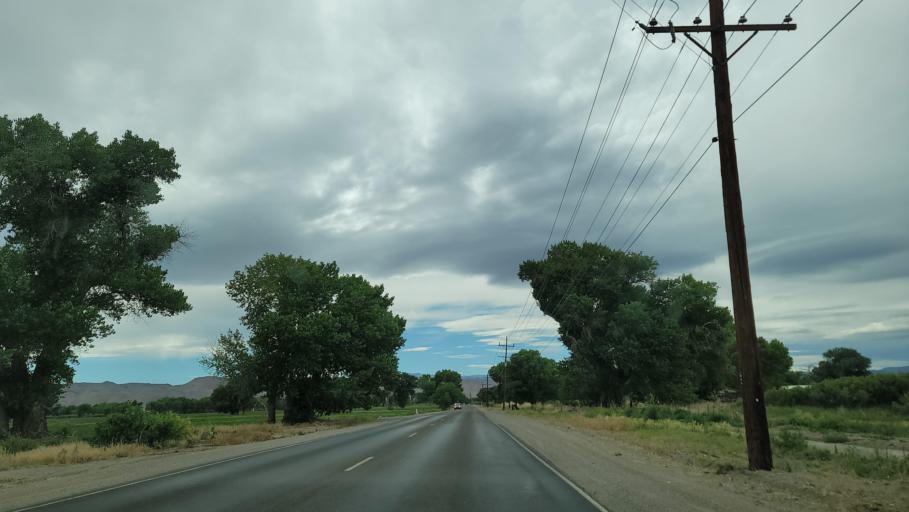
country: US
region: Nevada
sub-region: Lyon County
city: Yerington
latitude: 39.0482
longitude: -119.1537
